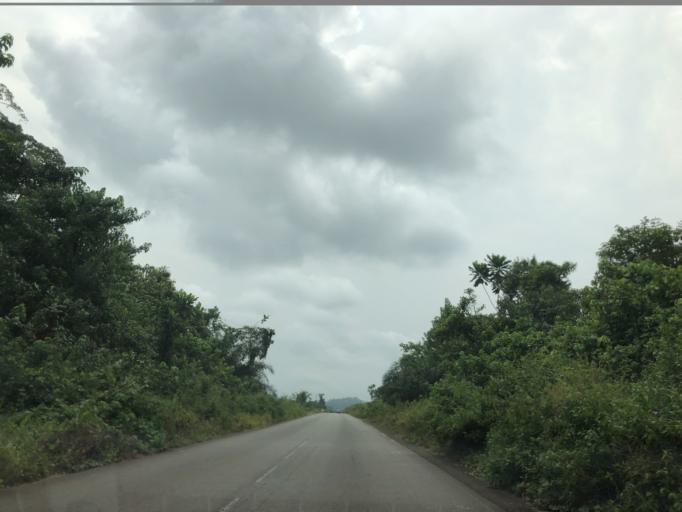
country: CM
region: Littoral
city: Edea
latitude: 3.6618
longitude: 10.1125
